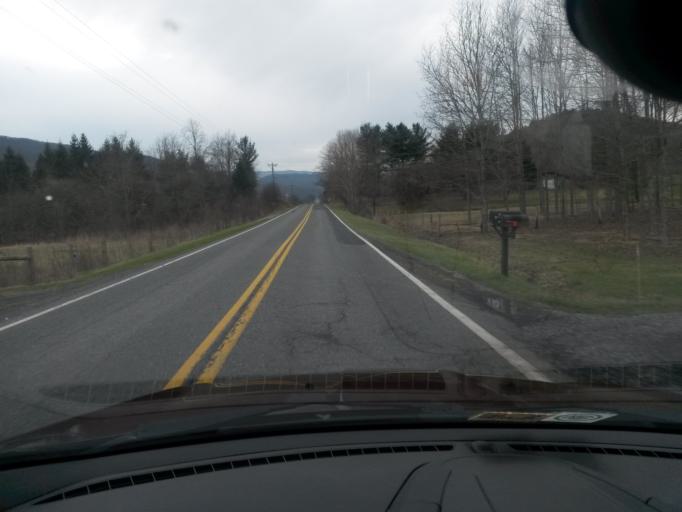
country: US
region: Virginia
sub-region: Highland County
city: Monterey
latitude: 38.2657
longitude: -79.6735
